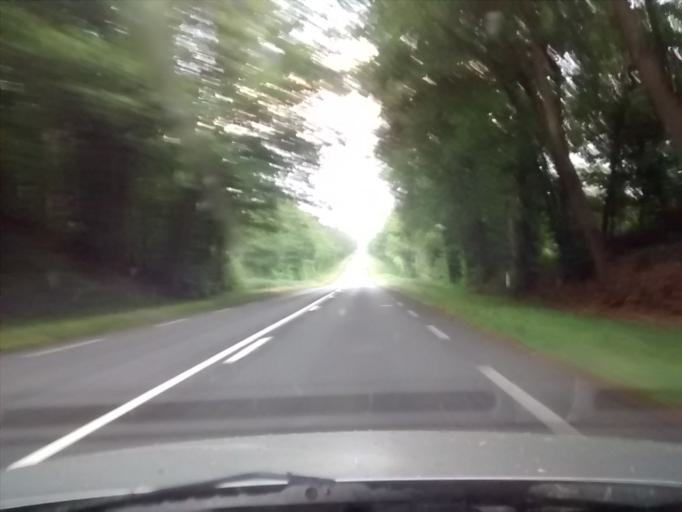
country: FR
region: Pays de la Loire
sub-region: Departement de la Sarthe
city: Le Breil-sur-Merize
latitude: 47.9944
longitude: 0.4533
